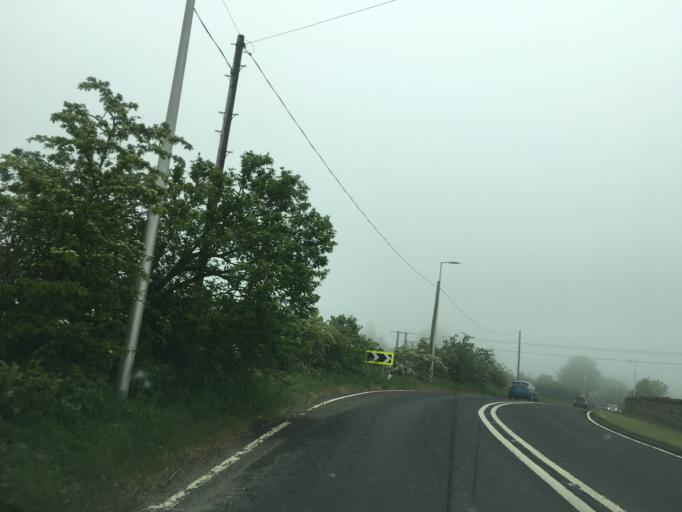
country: GB
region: Scotland
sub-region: Midlothian
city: Penicuik
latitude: 55.8298
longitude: -3.2018
